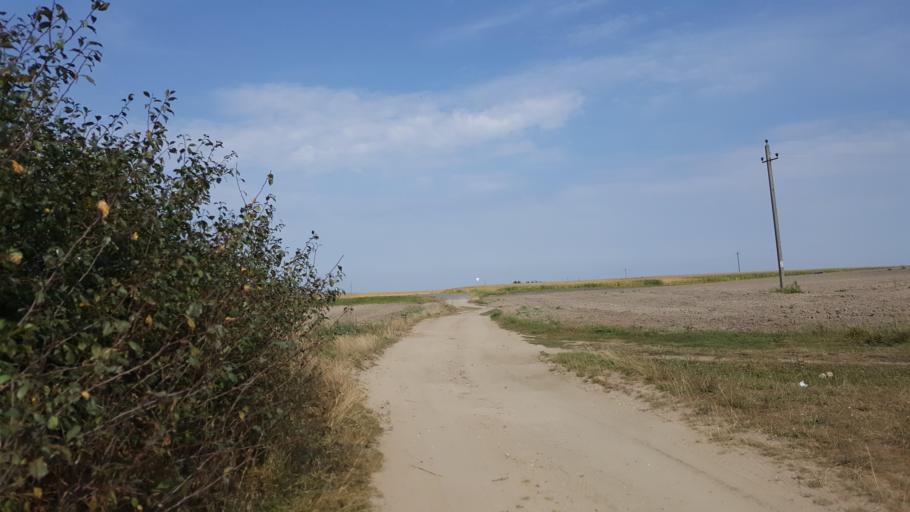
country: BY
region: Brest
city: Kamyanyets
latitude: 52.4064
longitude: 23.7867
